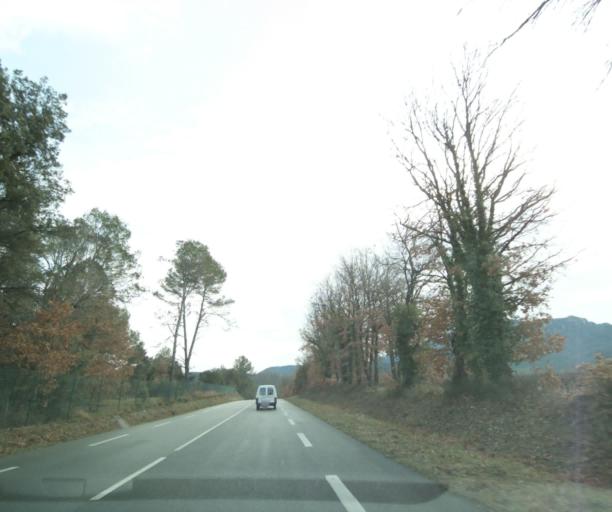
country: FR
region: Provence-Alpes-Cote d'Azur
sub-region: Departement du Var
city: Tourves
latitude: 43.3962
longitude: 5.9706
